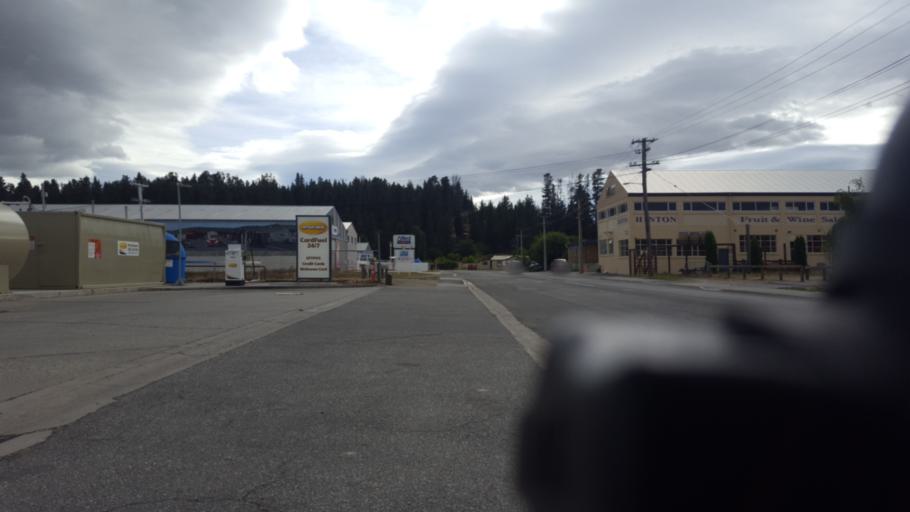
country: NZ
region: Otago
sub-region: Queenstown-Lakes District
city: Wanaka
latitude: -45.2461
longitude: 169.3947
